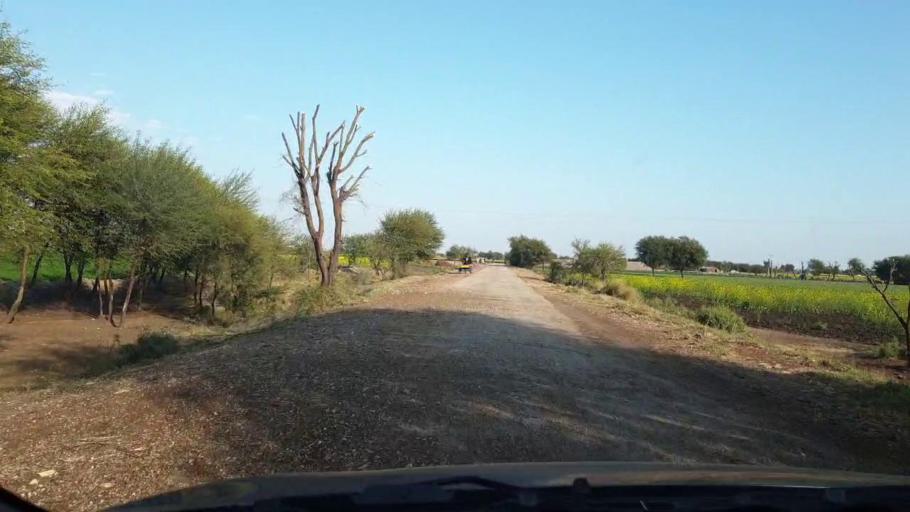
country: PK
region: Sindh
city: Jhol
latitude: 25.9623
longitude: 68.8583
